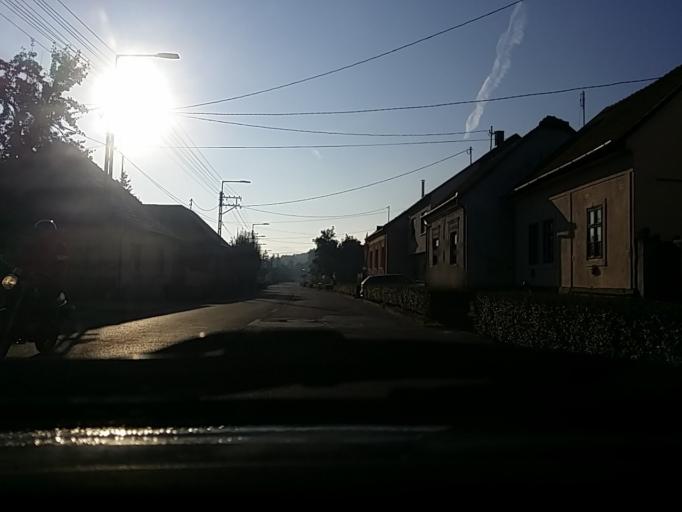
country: HU
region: Komarom-Esztergom
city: Pilismarot
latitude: 47.7868
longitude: 18.8711
